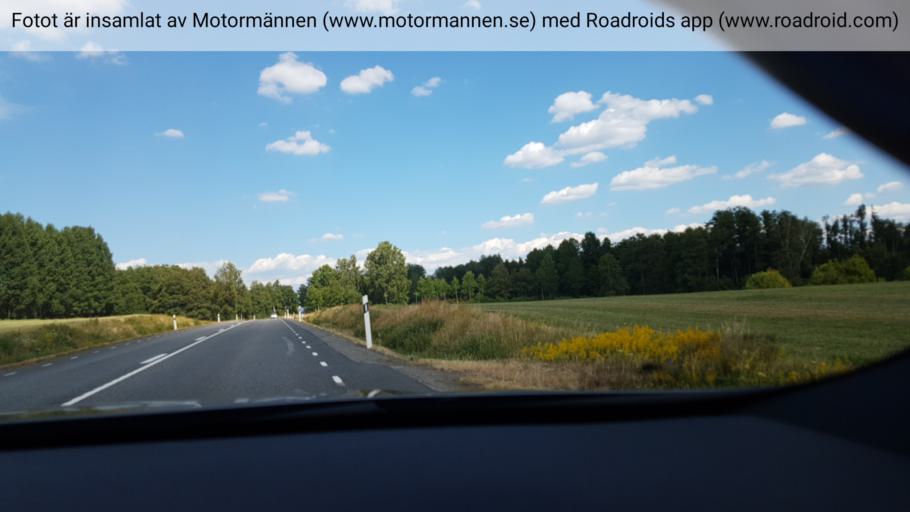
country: SE
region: Joenkoeping
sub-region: Vetlanda Kommun
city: Landsbro
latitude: 57.4024
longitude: 14.9331
